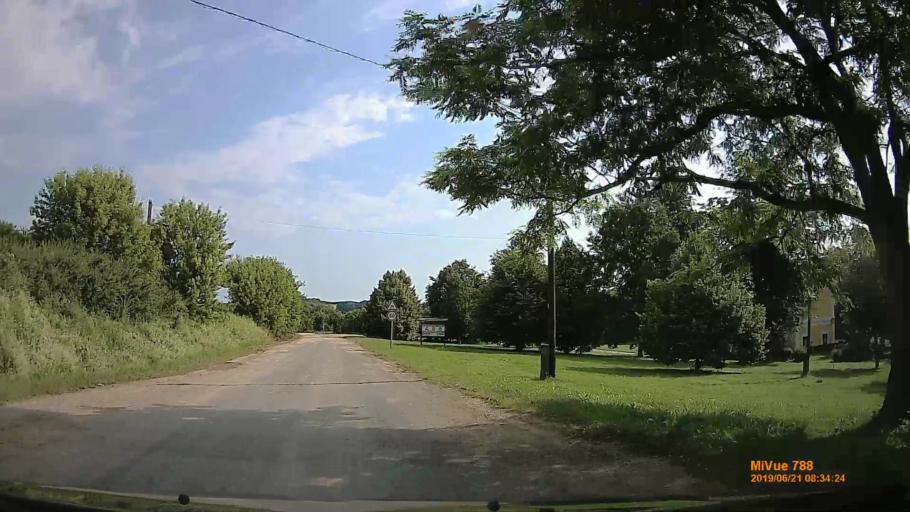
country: HU
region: Baranya
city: Buekkoesd
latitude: 46.1674
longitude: 17.8880
